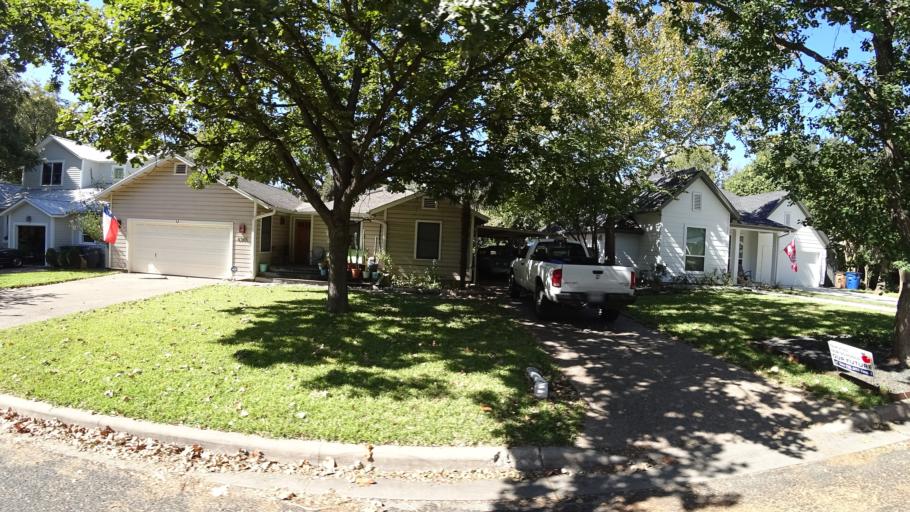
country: US
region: Texas
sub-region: Travis County
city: Austin
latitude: 30.3231
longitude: -97.7438
